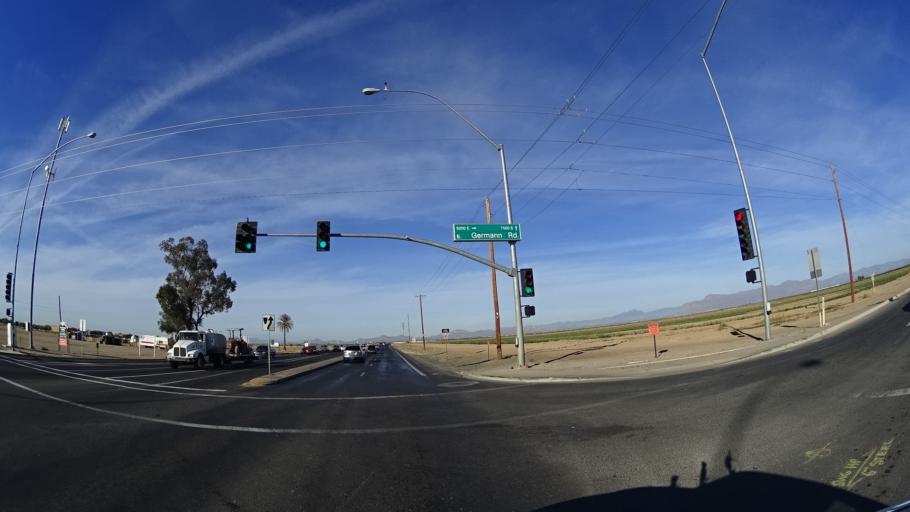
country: US
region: Arizona
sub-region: Maricopa County
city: Queen Creek
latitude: 33.2776
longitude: -111.6348
